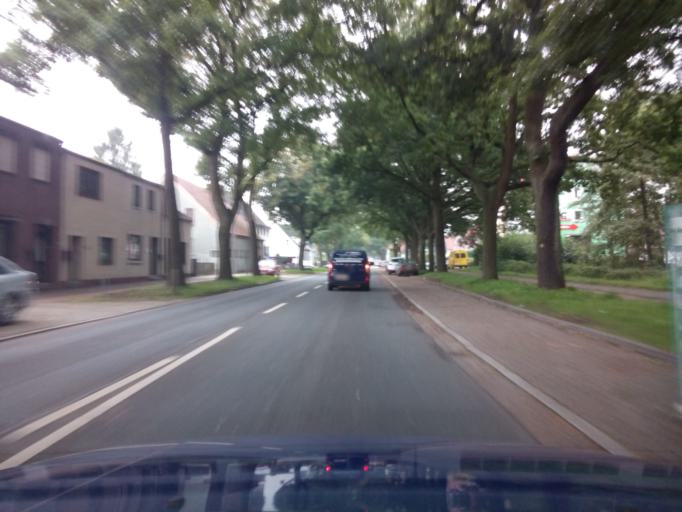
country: DE
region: Bremen
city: Bremen
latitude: 53.0379
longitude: 8.8129
